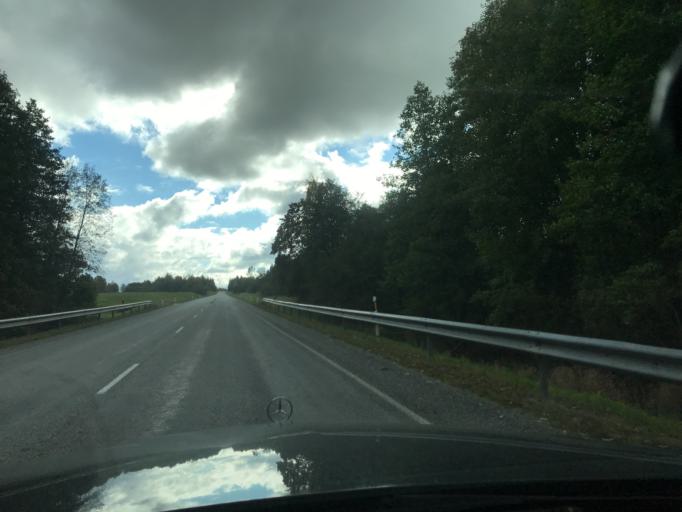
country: RU
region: Pskov
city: Pechory
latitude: 57.7069
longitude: 27.3226
